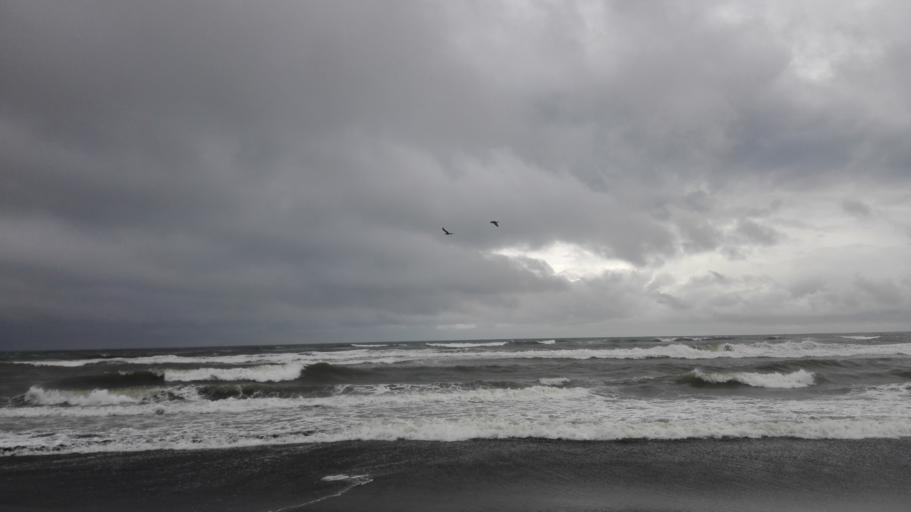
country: GE
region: Guria
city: Urek'i
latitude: 41.9831
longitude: 41.7594
